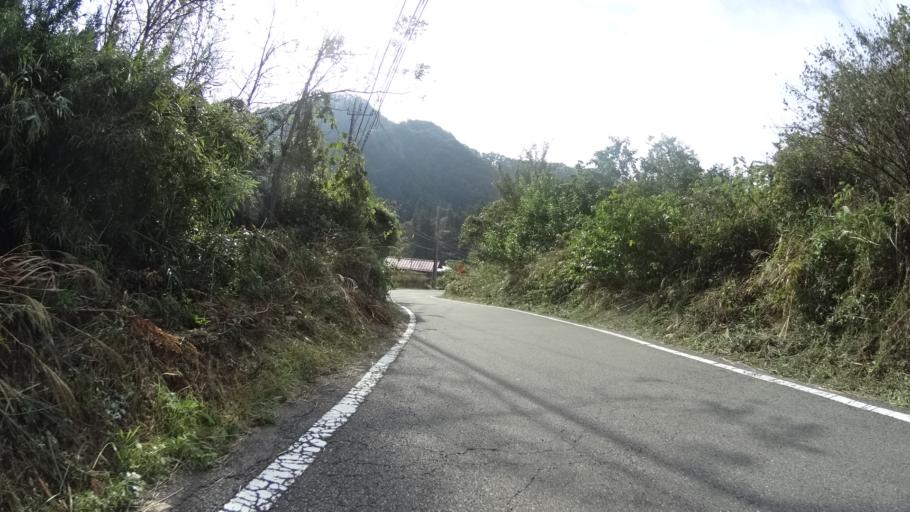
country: JP
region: Yamanashi
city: Otsuki
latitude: 35.6179
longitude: 139.0175
